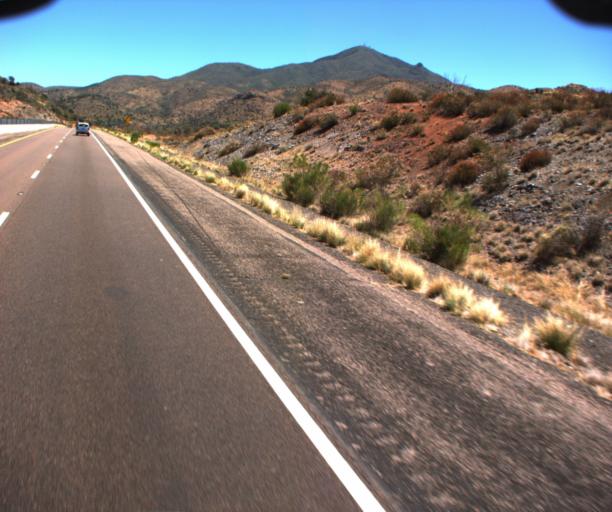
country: US
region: Arizona
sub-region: Gila County
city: Tonto Basin
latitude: 33.8740
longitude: -111.4614
